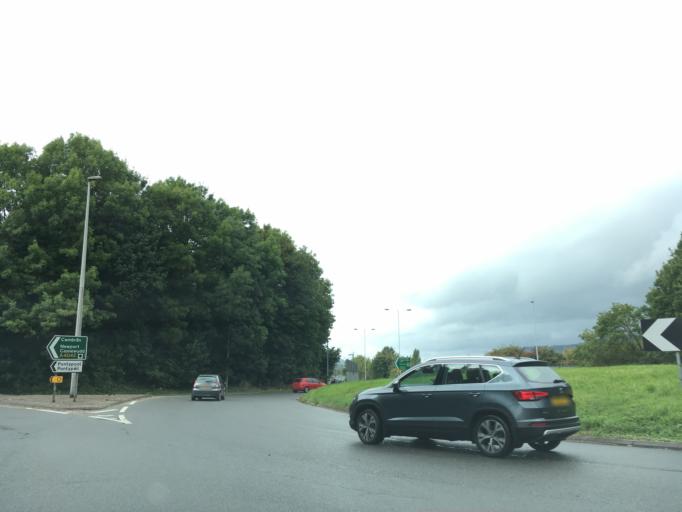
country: GB
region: Wales
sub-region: Monmouthshire
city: Abergavenny
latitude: 51.8096
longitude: -3.0093
